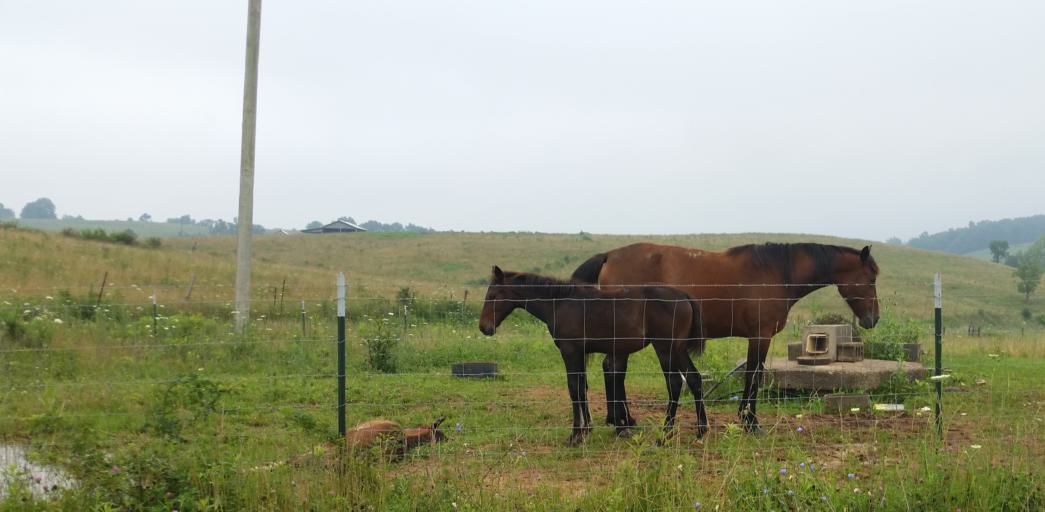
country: US
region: Ohio
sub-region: Gallia County
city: Gallipolis
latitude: 38.7547
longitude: -82.3581
